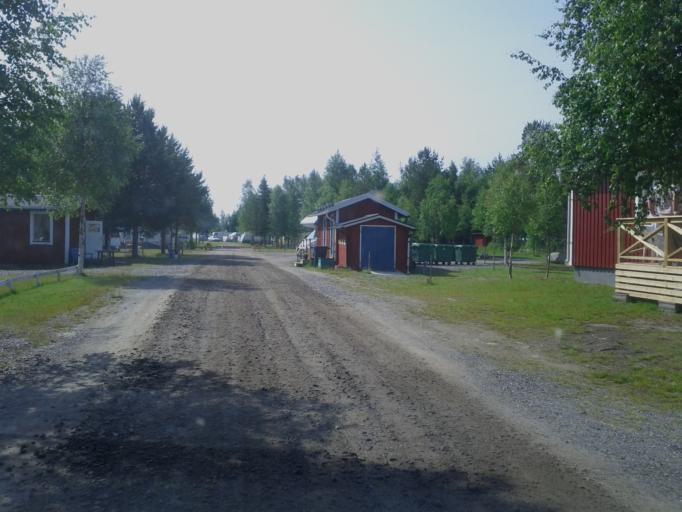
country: SE
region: Vaesterbotten
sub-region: Robertsfors Kommun
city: Robertsfors
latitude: 64.1568
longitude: 20.9740
